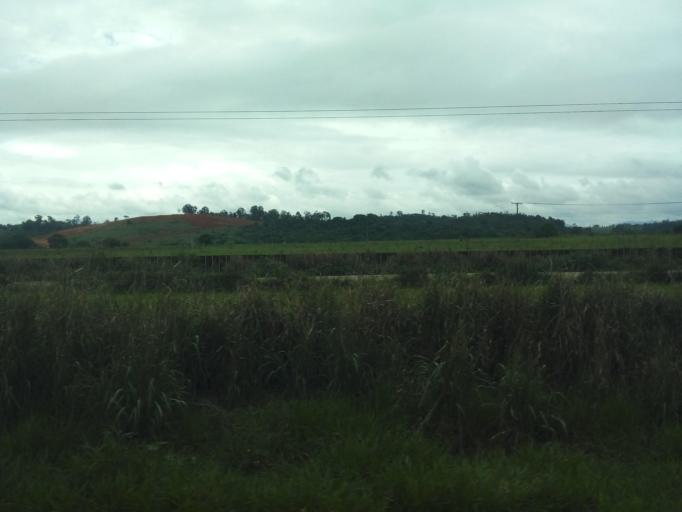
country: BR
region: Minas Gerais
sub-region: Ipatinga
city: Ipatinga
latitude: -19.4680
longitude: -42.4790
